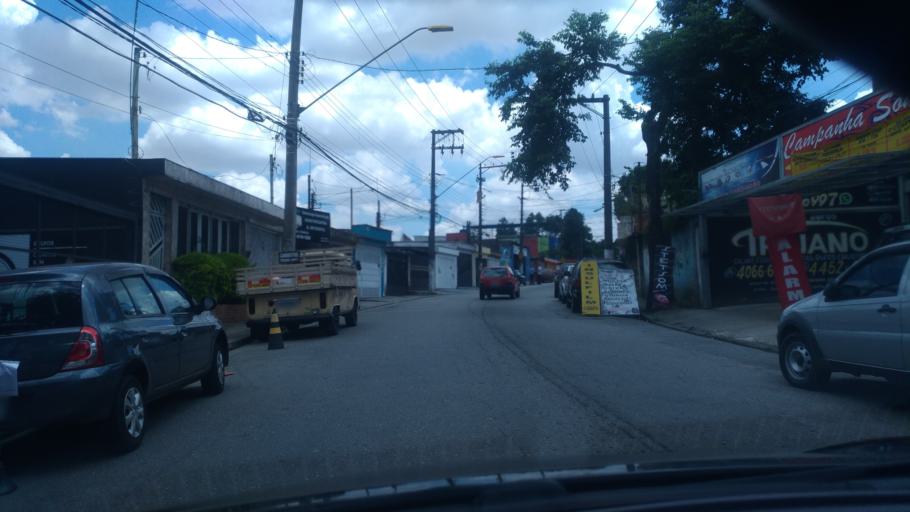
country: BR
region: Sao Paulo
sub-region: Santo Andre
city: Santo Andre
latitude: -23.6998
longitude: -46.5044
